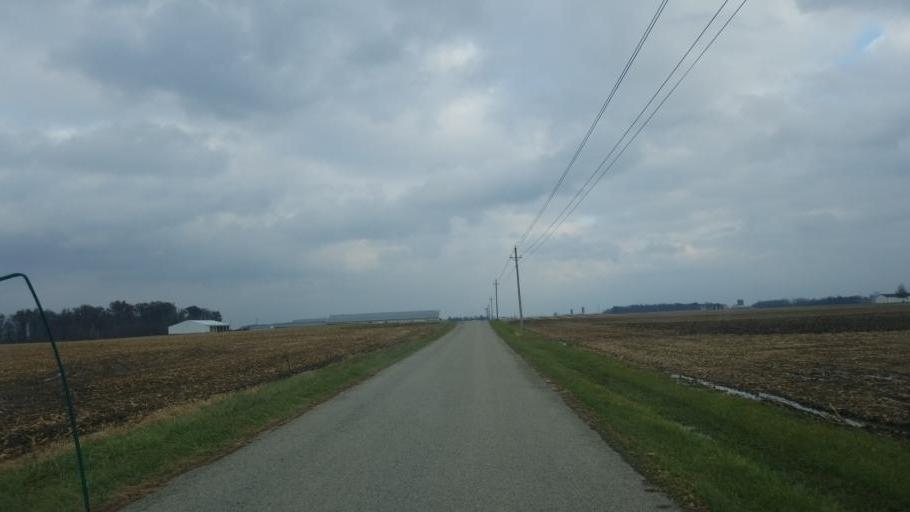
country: US
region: Indiana
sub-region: Adams County
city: Geneva
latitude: 40.5134
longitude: -84.8635
